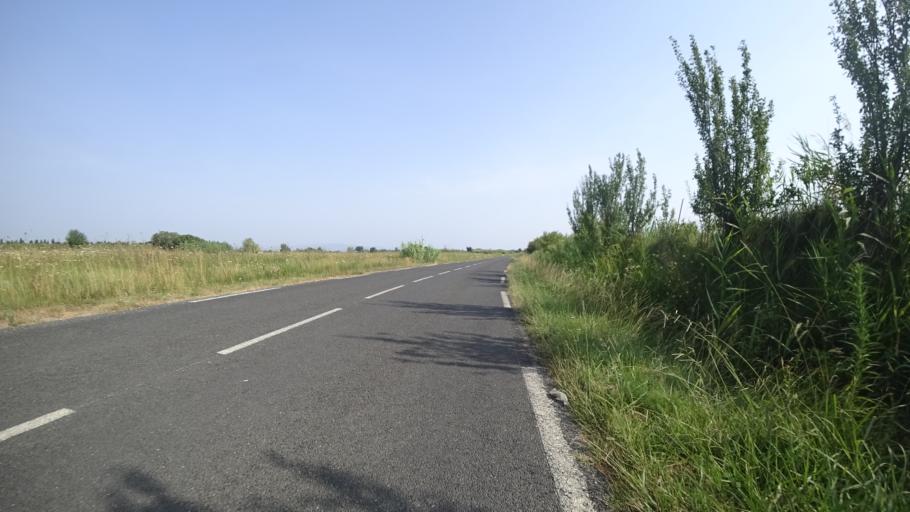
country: FR
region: Languedoc-Roussillon
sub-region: Departement des Pyrenees-Orientales
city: Villelongue-de-la-Salanque
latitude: 42.7347
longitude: 2.9892
